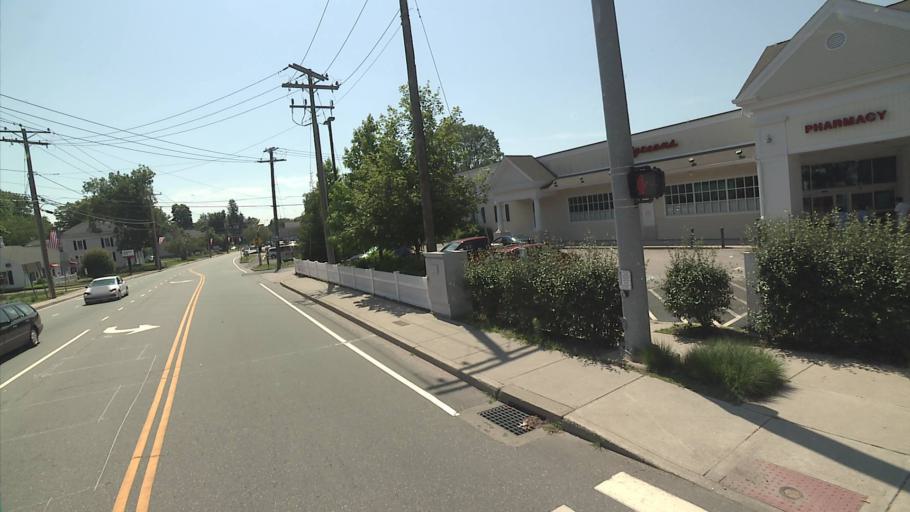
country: US
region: Connecticut
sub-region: Middlesex County
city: Westbrook Center
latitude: 41.2855
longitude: -72.4481
